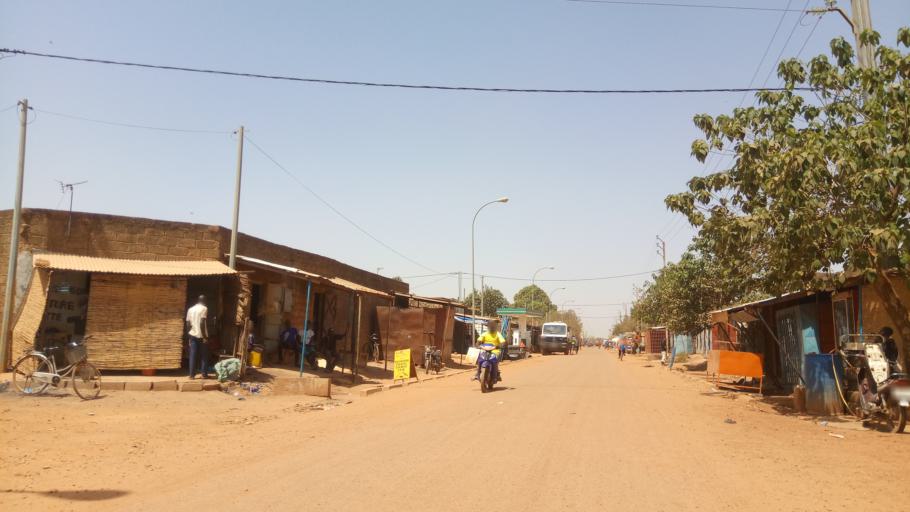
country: BF
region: Centre
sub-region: Kadiogo Province
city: Ouagadougou
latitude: 12.3919
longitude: -1.5626
